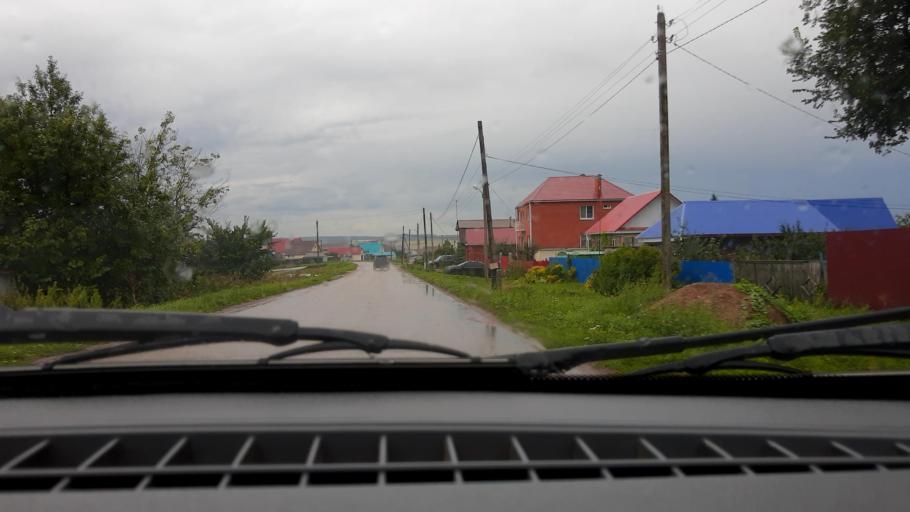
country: RU
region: Bashkortostan
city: Avdon
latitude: 54.8163
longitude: 55.6954
